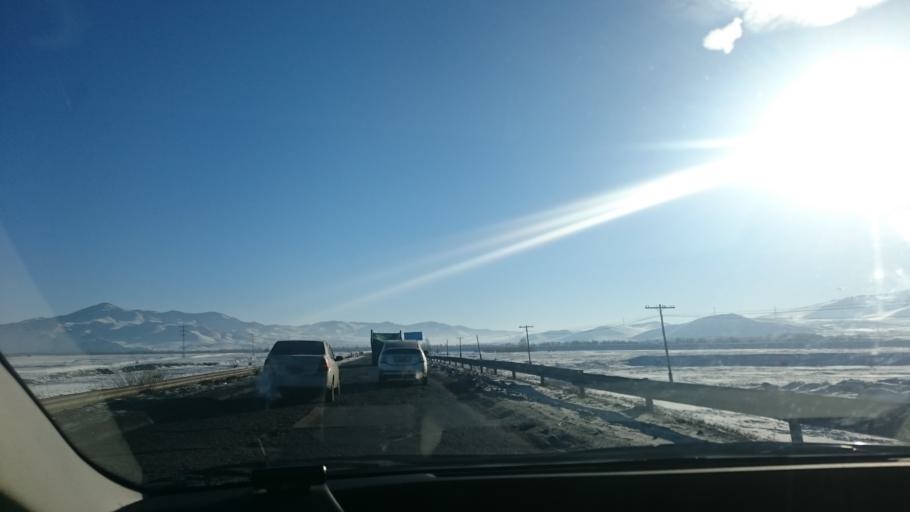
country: MN
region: Ulaanbaatar
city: Ulaanbaatar
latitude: 47.8999
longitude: 107.0369
